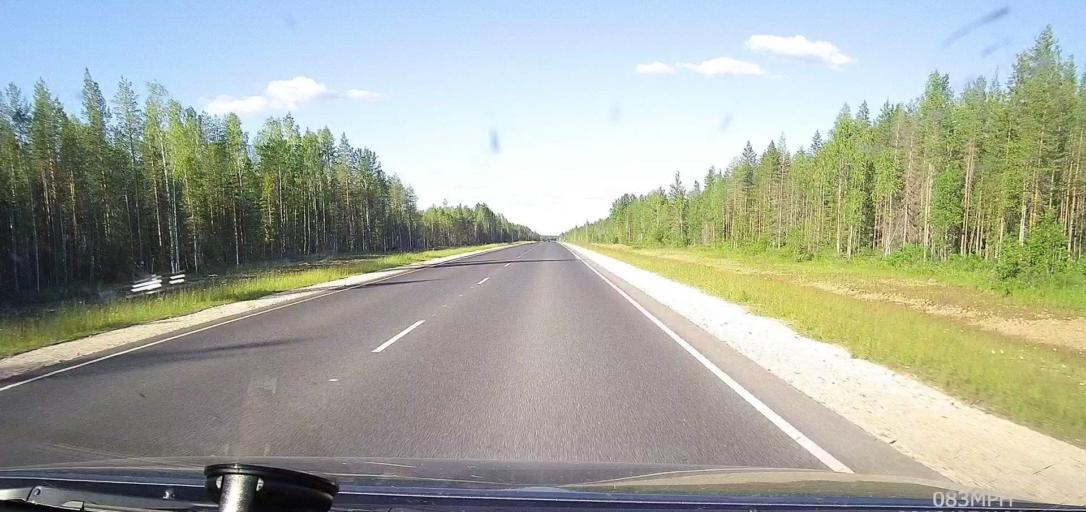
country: RU
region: Arkhangelskaya
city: Yemtsa
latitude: 63.1351
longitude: 40.4663
